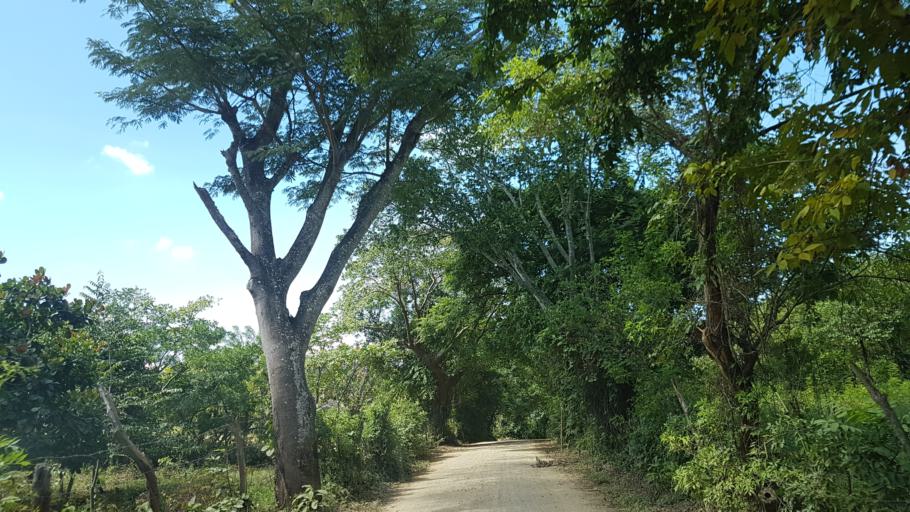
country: HN
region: El Paraiso
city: Oropoli
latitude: 13.7368
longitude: -86.6984
